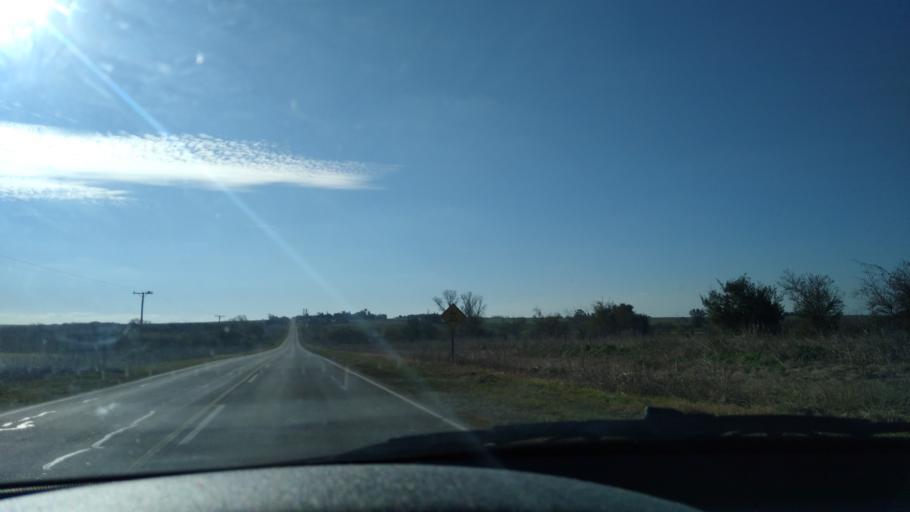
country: AR
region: Entre Rios
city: Aranguren
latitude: -32.3789
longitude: -60.3380
